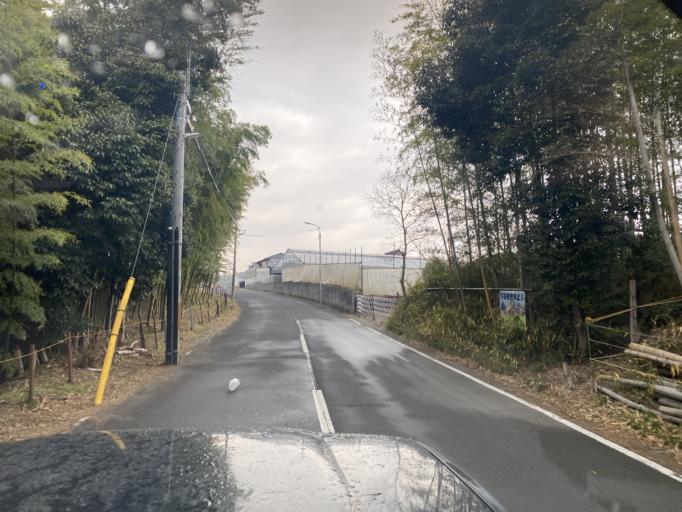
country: JP
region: Kyoto
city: Tanabe
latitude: 34.8135
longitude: 135.7614
